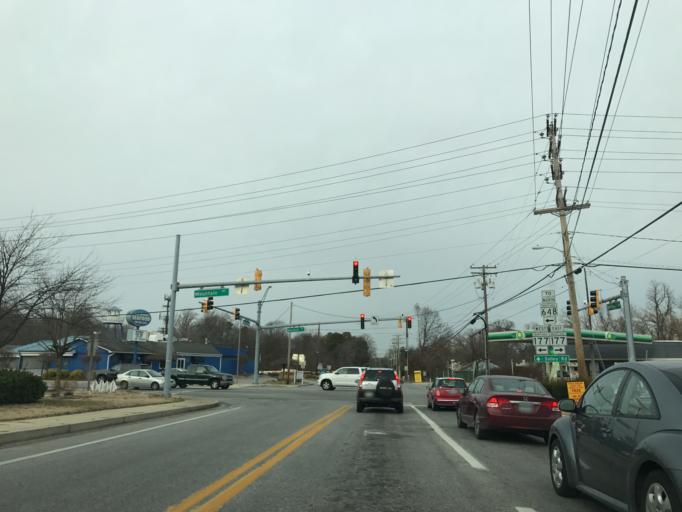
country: US
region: Maryland
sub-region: Anne Arundel County
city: Green Haven
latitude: 39.1310
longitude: -76.5631
